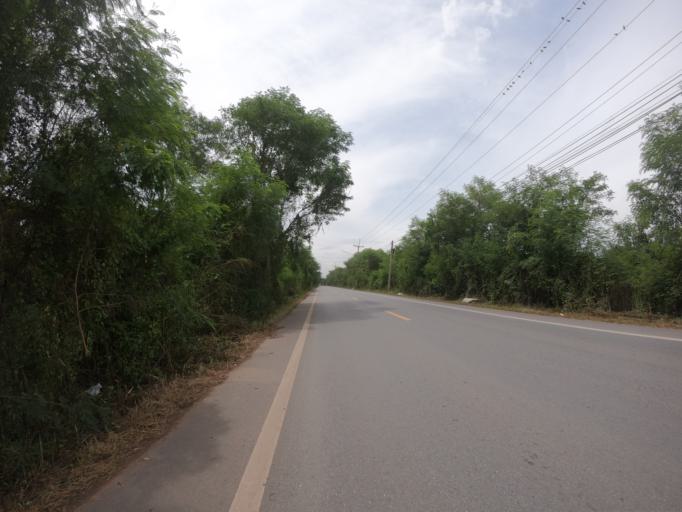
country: TH
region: Pathum Thani
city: Nong Suea
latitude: 14.0640
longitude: 100.8716
